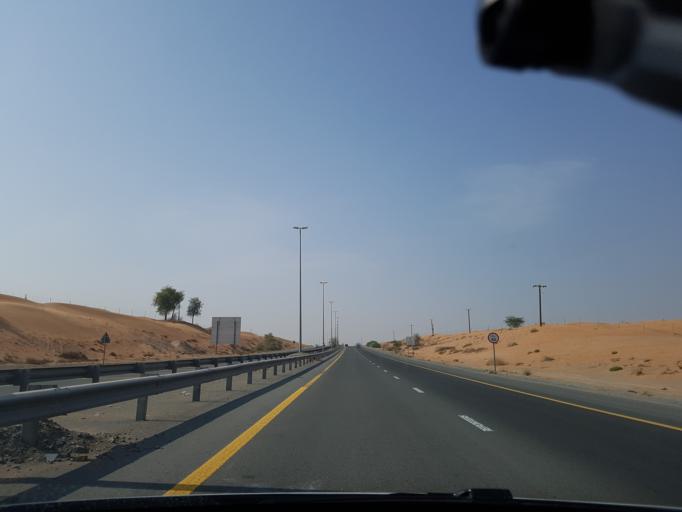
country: AE
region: Umm al Qaywayn
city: Umm al Qaywayn
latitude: 25.5166
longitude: 55.7438
